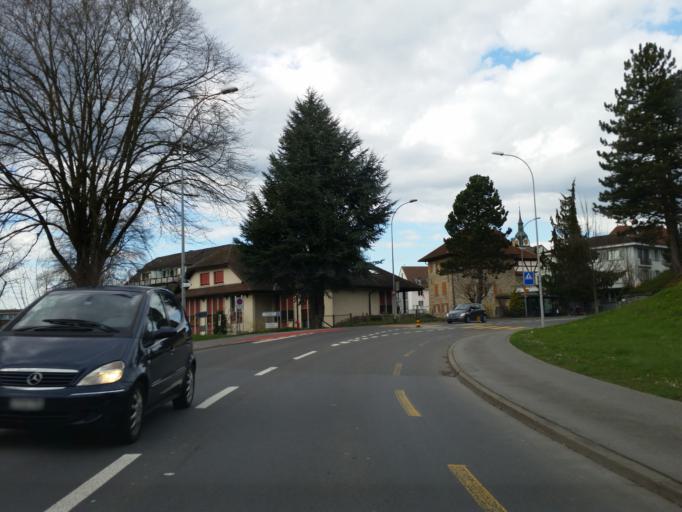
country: CH
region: Lucerne
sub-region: Sursee District
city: Sempach
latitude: 47.1336
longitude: 8.1914
